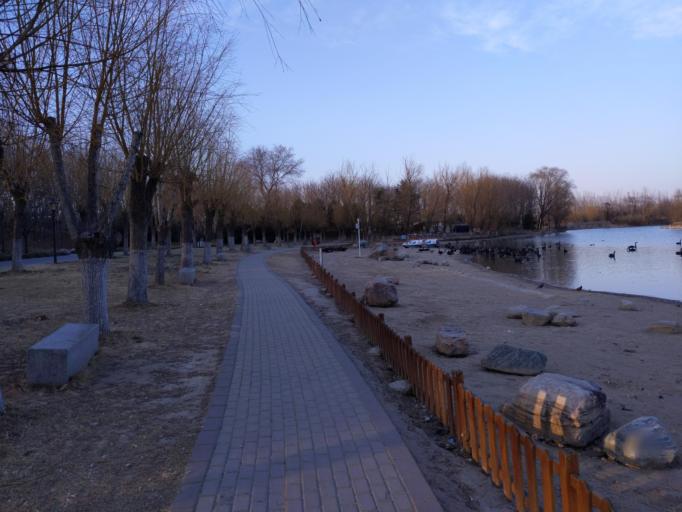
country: CN
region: Henan Sheng
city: Puyang
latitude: 35.7831
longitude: 114.9511
